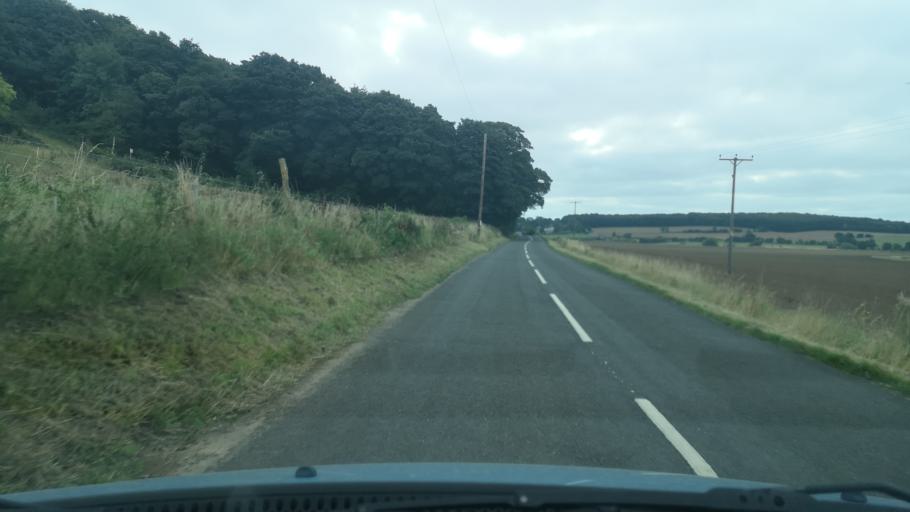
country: GB
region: England
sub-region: City and Borough of Wakefield
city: Darrington
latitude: 53.6573
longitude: -1.2779
